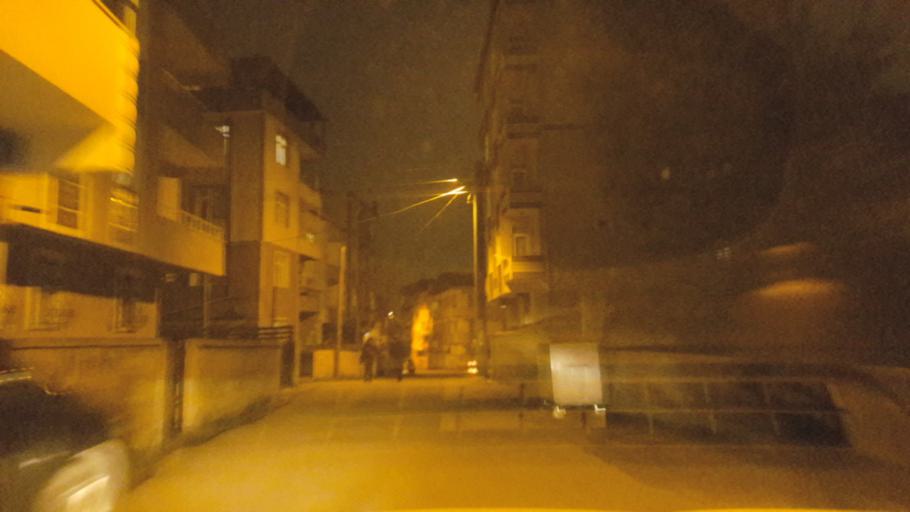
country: TR
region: Kocaeli
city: Darica
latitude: 40.7771
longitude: 29.4039
